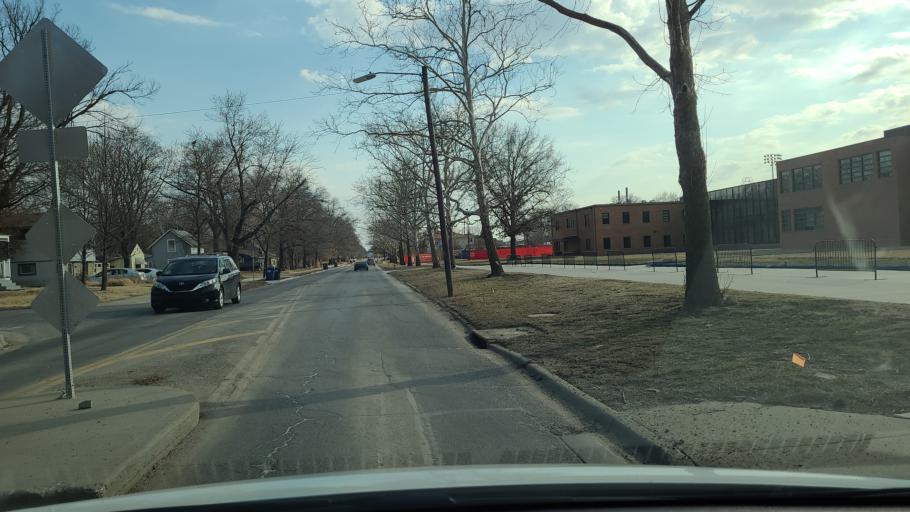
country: US
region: Kansas
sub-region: Douglas County
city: Lawrence
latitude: 38.9484
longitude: -95.2419
